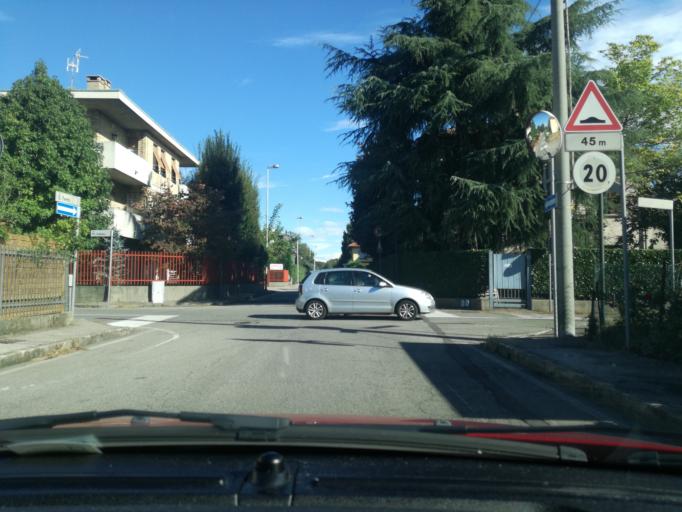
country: IT
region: Lombardy
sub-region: Provincia di Monza e Brianza
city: Meda
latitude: 45.6575
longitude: 9.1741
